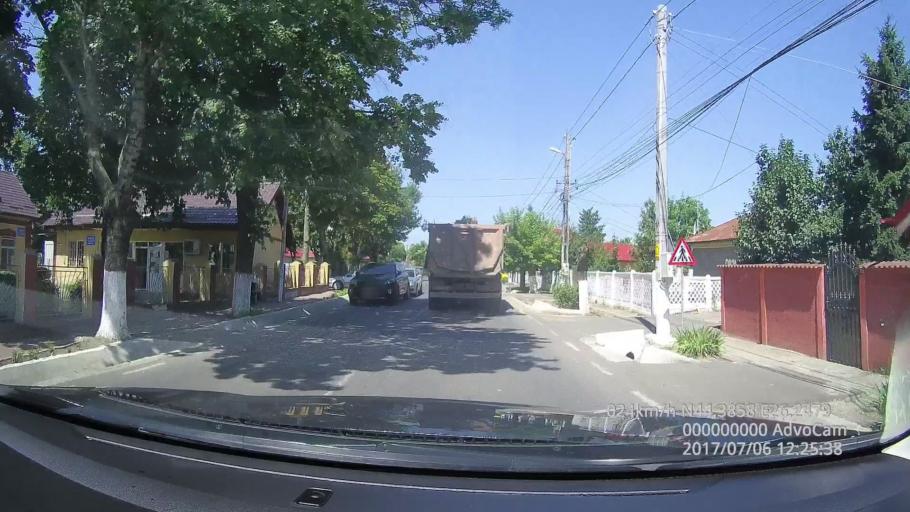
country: RO
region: Ilfov
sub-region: Comuna Glina
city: Glina
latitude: 44.3859
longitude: 26.2478
